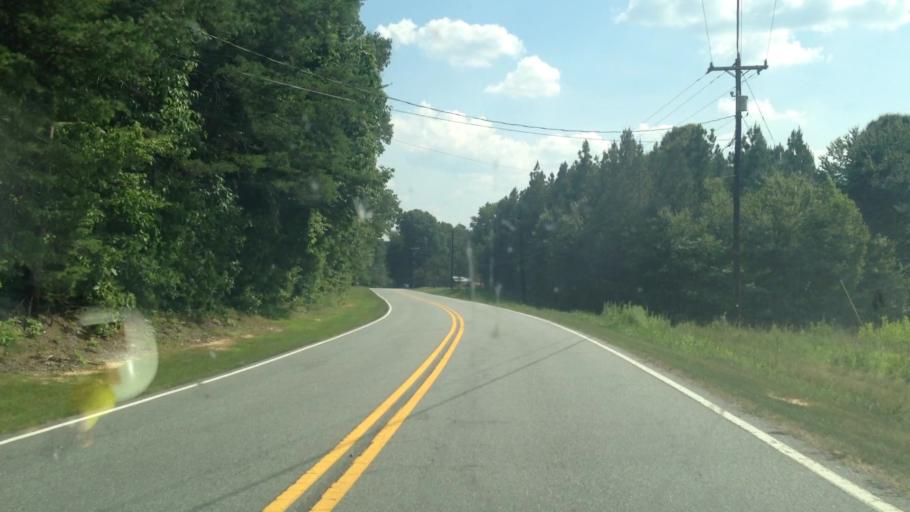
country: US
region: North Carolina
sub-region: Stokes County
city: Walnut Cove
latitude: 36.2336
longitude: -80.1098
